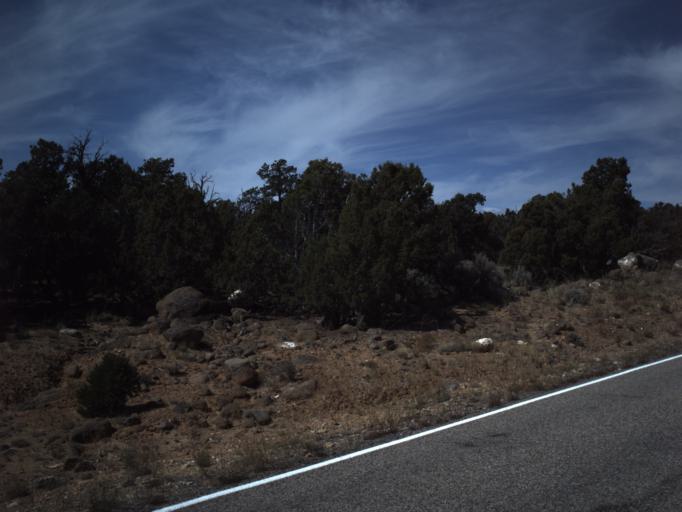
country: US
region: Utah
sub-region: Wayne County
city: Loa
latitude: 37.8613
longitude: -111.4379
